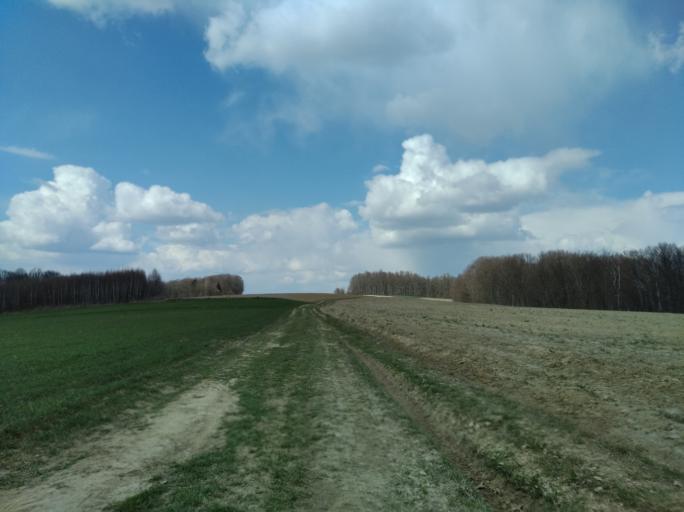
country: PL
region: Subcarpathian Voivodeship
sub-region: Powiat strzyzowski
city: Strzyzow
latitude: 49.9168
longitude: 21.7454
